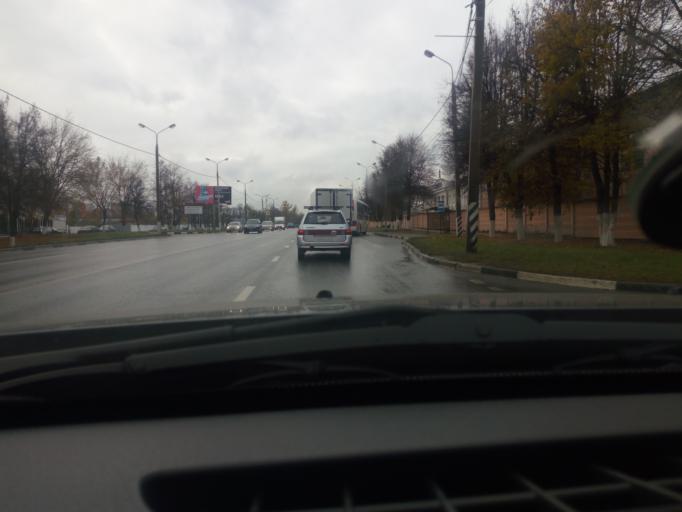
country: RU
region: Moskovskaya
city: Domodedovo
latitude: 55.4469
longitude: 37.7643
